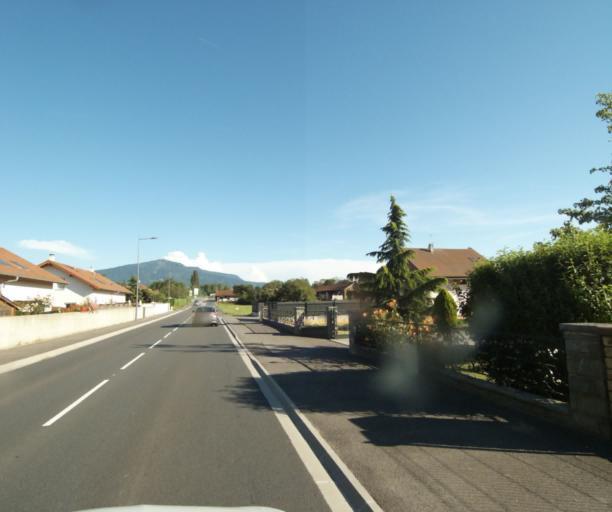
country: FR
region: Rhone-Alpes
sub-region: Departement de la Haute-Savoie
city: Douvaine
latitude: 46.3012
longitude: 6.3037
